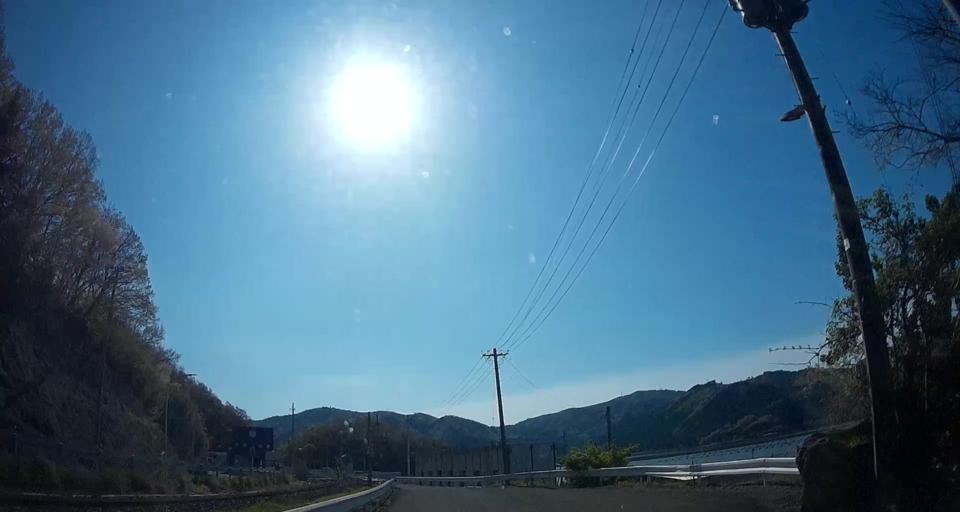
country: JP
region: Miyagi
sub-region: Oshika Gun
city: Onagawa Cho
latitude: 38.4336
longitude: 141.4103
